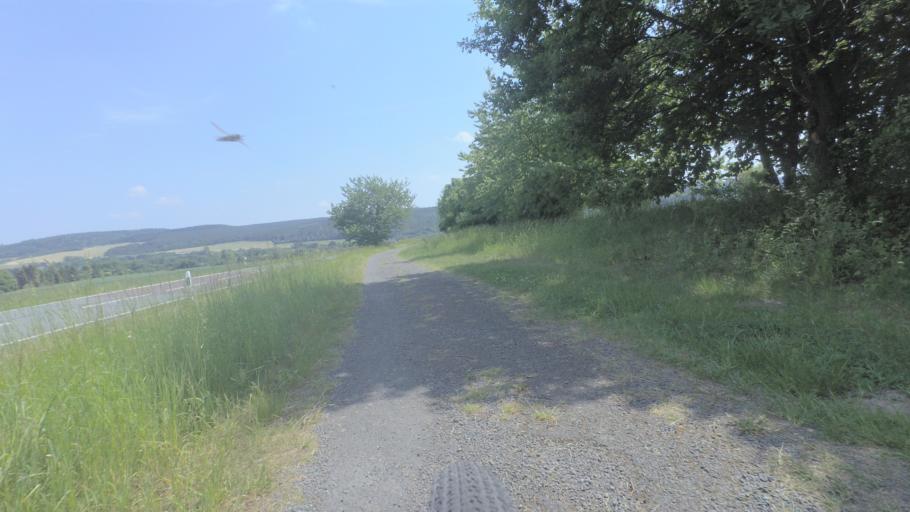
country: DE
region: Saxony-Anhalt
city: Ballenstedt
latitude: 51.7083
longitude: 11.2827
